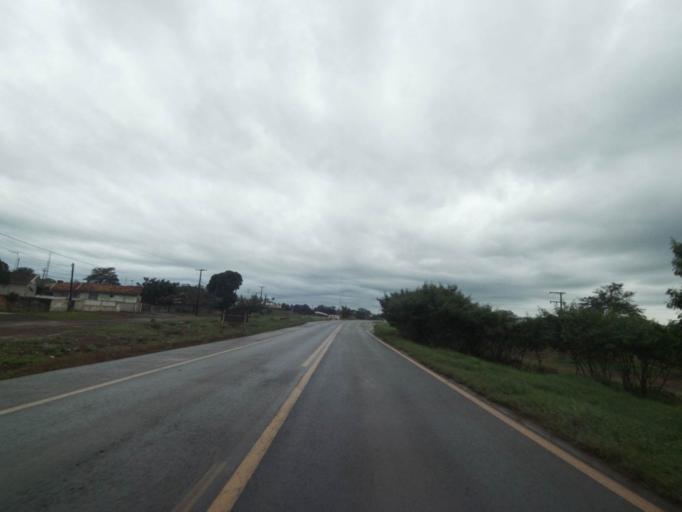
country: BR
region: Parana
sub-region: Toledo
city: Toledo
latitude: -24.6987
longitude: -53.7366
